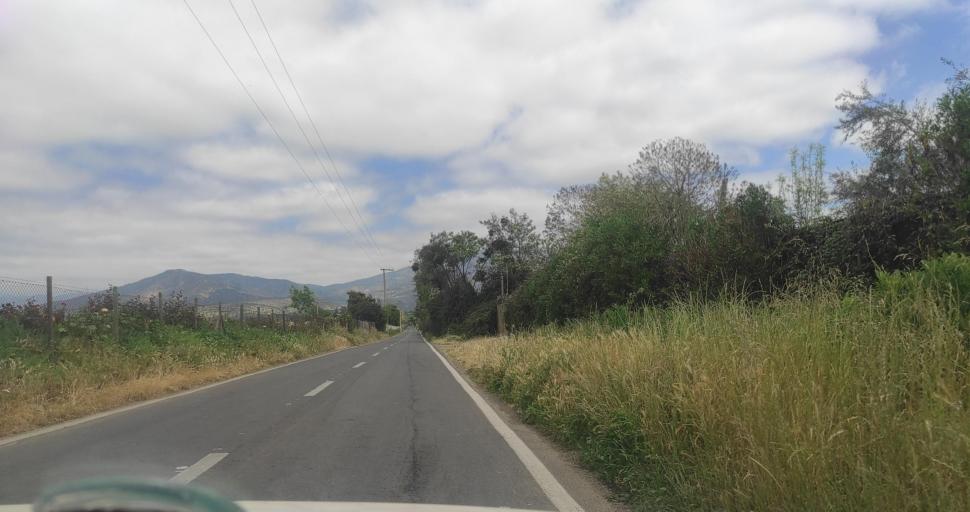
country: CL
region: Valparaiso
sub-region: Provincia de Marga Marga
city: Limache
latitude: -33.0254
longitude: -71.2283
